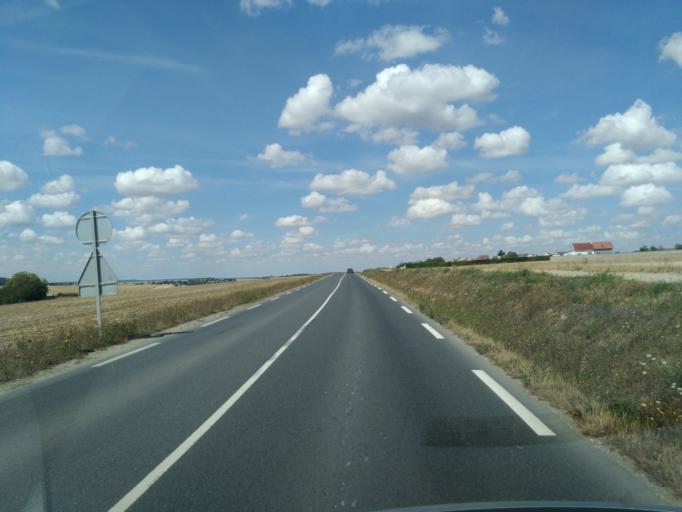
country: FR
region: Ile-de-France
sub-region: Departement des Yvelines
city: Plaisir
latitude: 48.8381
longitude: 1.9407
